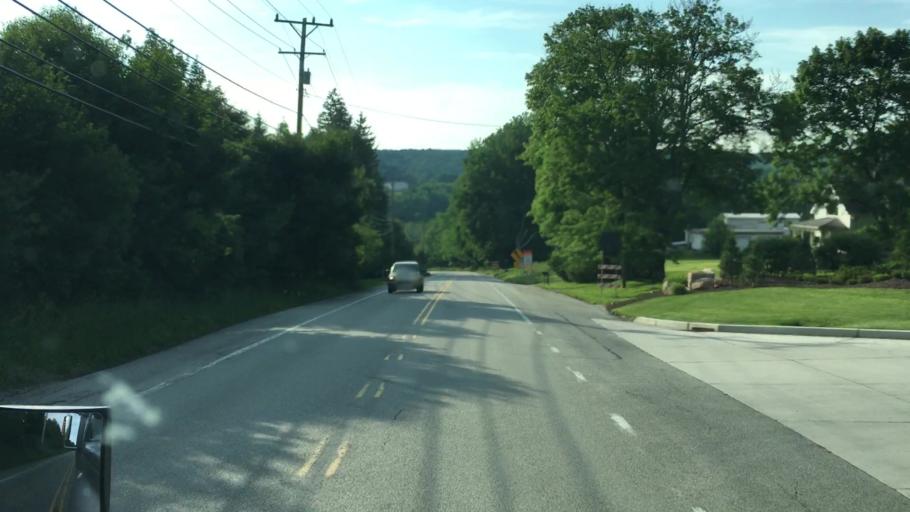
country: US
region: Pennsylvania
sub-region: Fayette County
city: Hopwood
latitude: 39.8034
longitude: -79.5560
